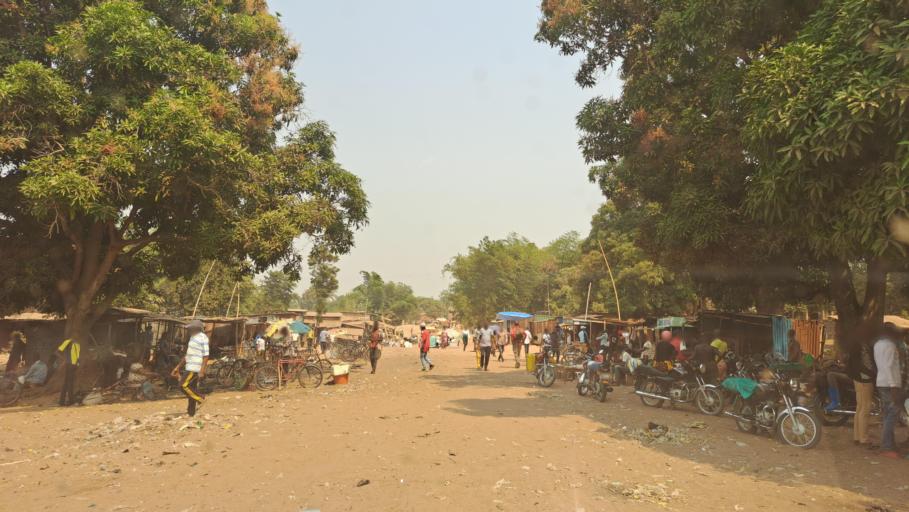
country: CD
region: Kasai-Oriental
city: Mbuji-Mayi
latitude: -6.1050
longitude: 23.5604
